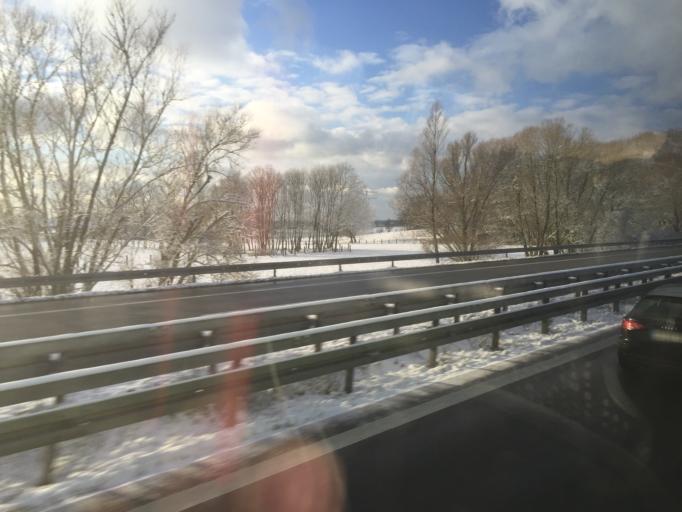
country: DE
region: Brandenburg
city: Gerdshagen
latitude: 53.2558
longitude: 12.1641
